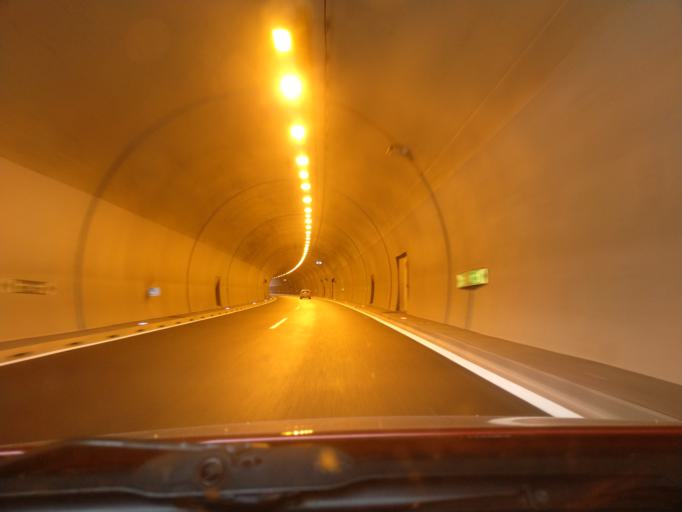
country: SI
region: Vipava
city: Vipava
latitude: 45.7955
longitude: 13.9873
